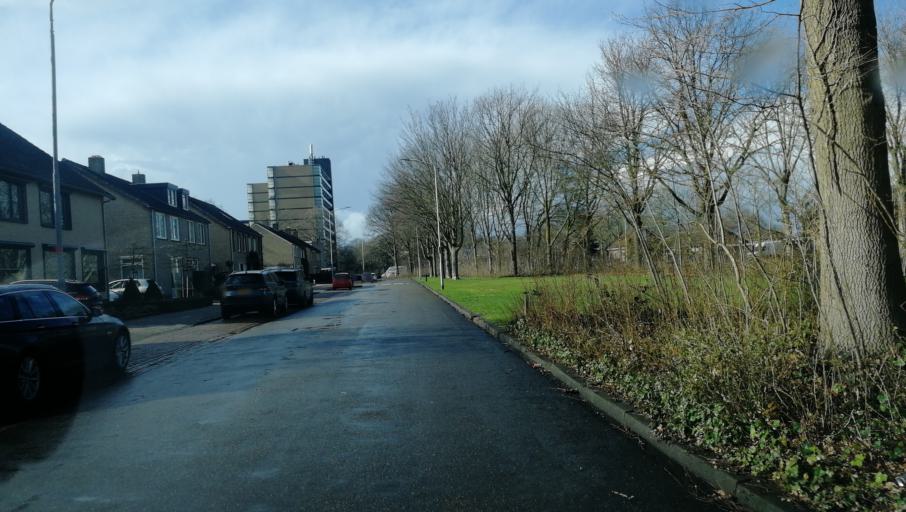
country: NL
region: Limburg
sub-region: Gemeente Venlo
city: Venlo
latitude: 51.3771
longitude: 6.1917
